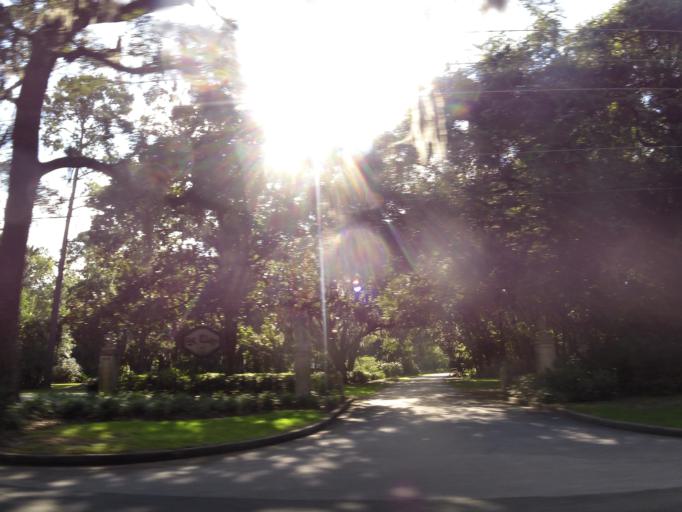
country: US
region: Georgia
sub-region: Glynn County
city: Saint Simon Mills
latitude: 31.1983
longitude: -81.3761
